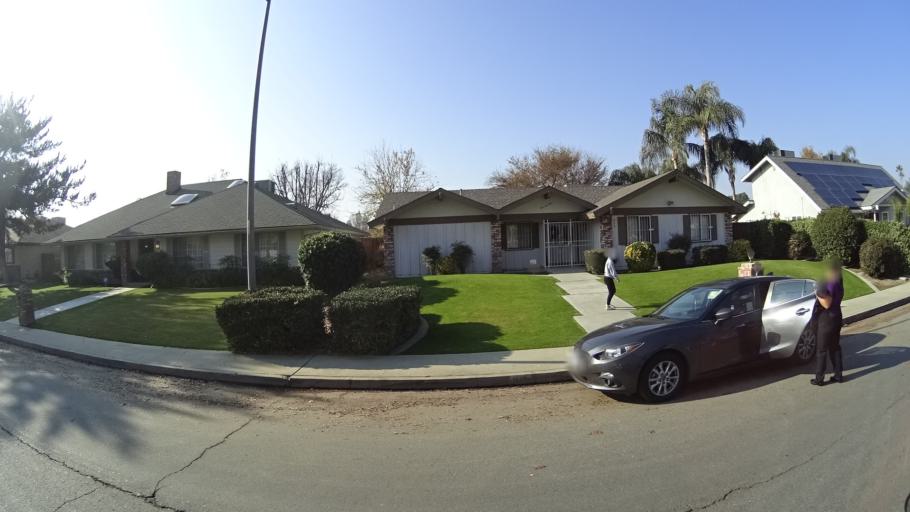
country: US
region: California
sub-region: Kern County
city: Bakersfield
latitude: 35.3610
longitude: -119.0545
